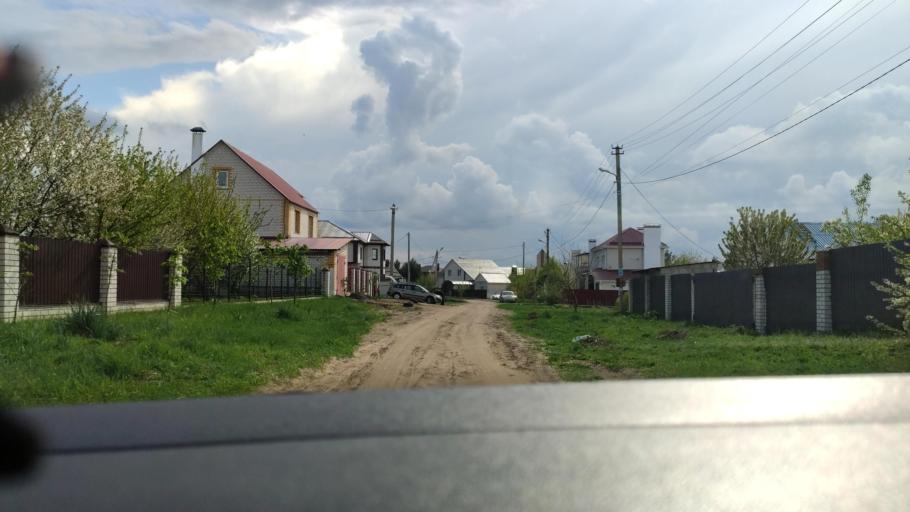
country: RU
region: Voronezj
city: Shilovo
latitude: 51.5669
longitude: 39.1098
